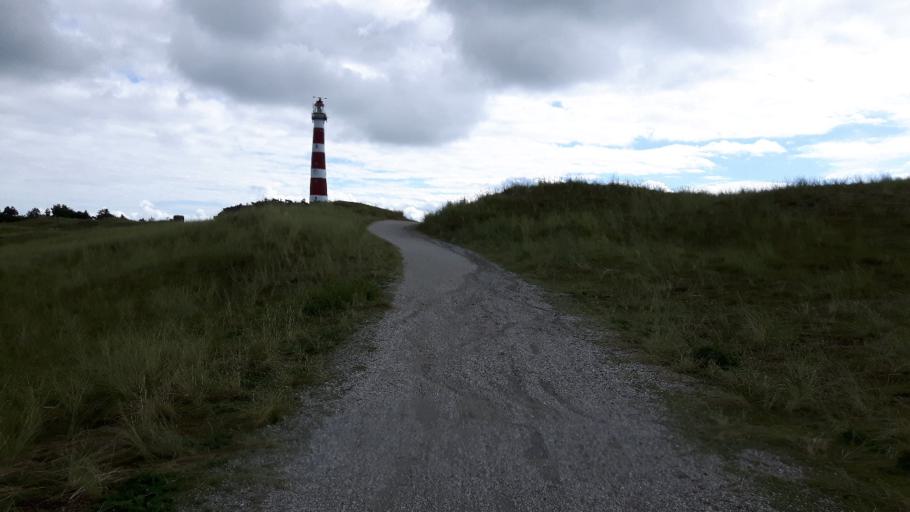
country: NL
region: Friesland
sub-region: Gemeente Ameland
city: Hollum
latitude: 53.4510
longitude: 5.6220
